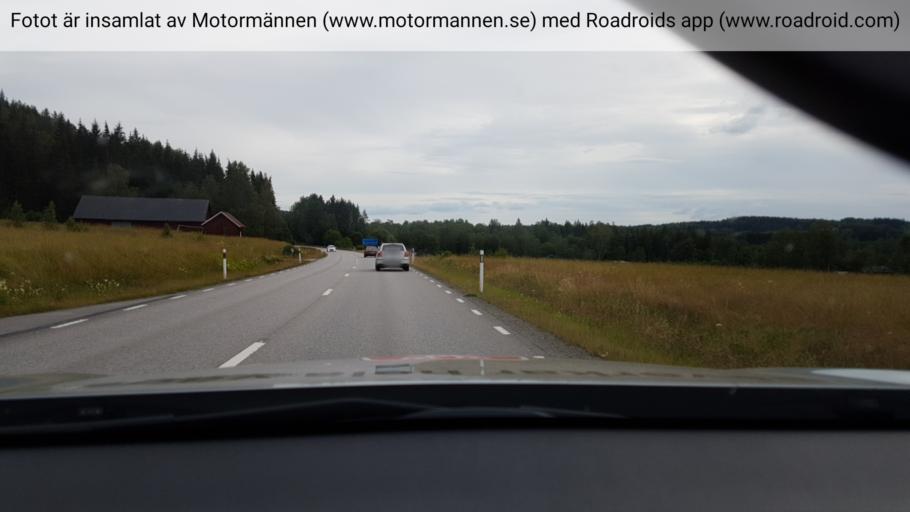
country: SE
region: Vaestra Goetaland
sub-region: Bengtsfors Kommun
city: Billingsfors
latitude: 58.9445
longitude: 12.2134
